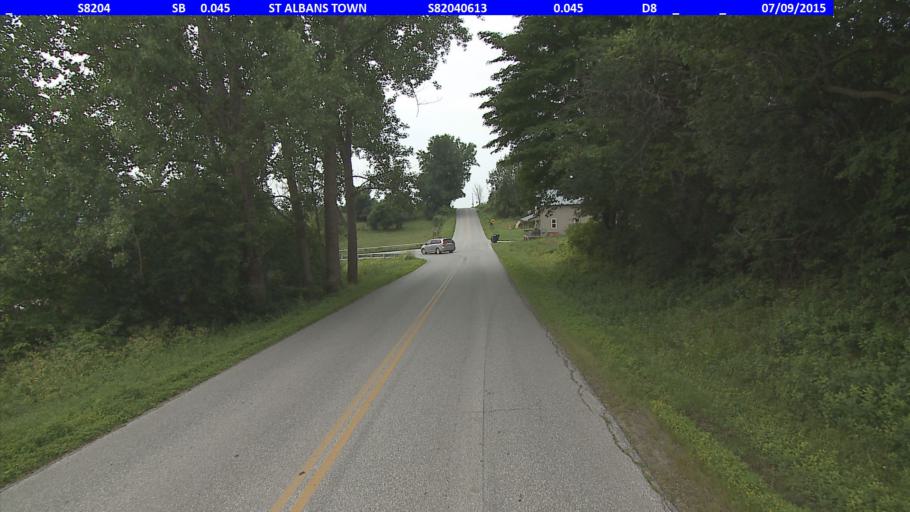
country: US
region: Vermont
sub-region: Franklin County
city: Saint Albans
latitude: 44.8035
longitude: -73.1130
